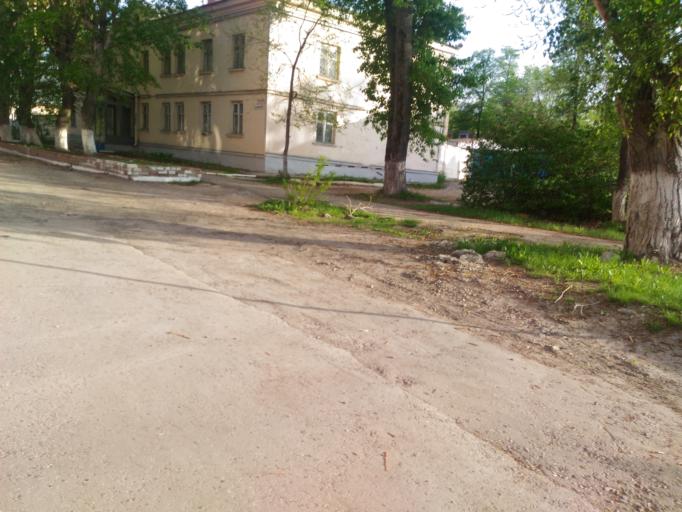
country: RU
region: Ulyanovsk
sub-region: Ulyanovskiy Rayon
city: Ulyanovsk
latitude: 54.2771
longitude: 48.3392
